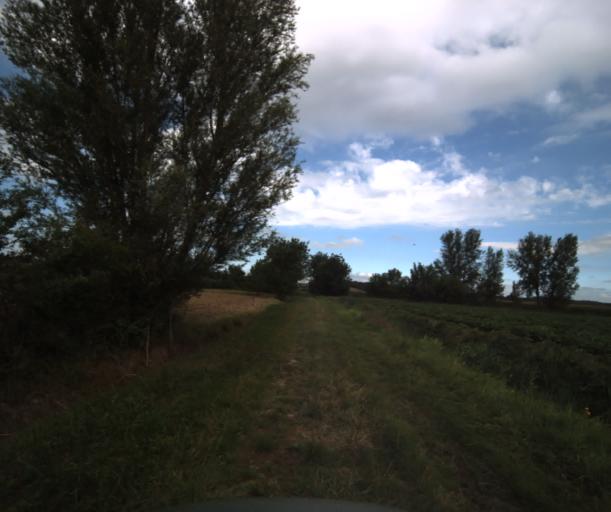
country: FR
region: Midi-Pyrenees
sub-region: Departement de la Haute-Garonne
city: Lherm
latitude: 43.3989
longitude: 1.2263
